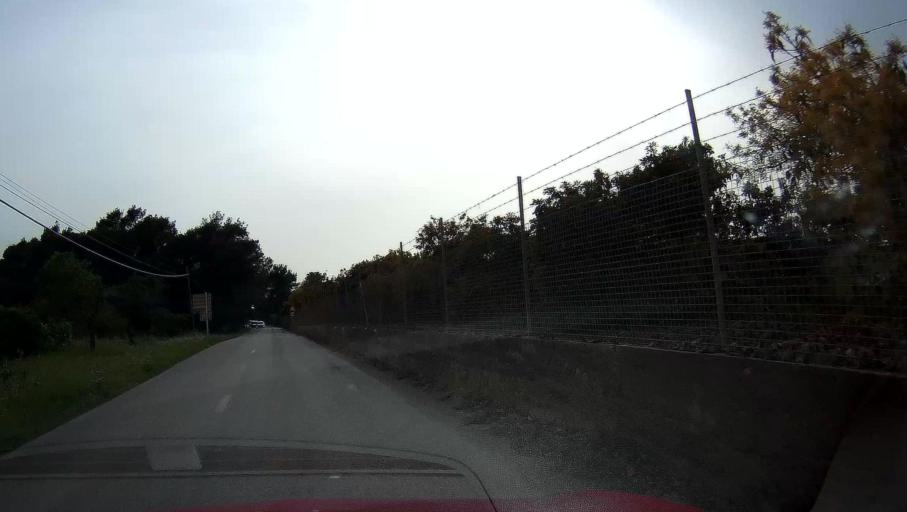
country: ES
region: Balearic Islands
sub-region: Illes Balears
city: Sant Joan de Labritja
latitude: 39.0377
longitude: 1.5428
